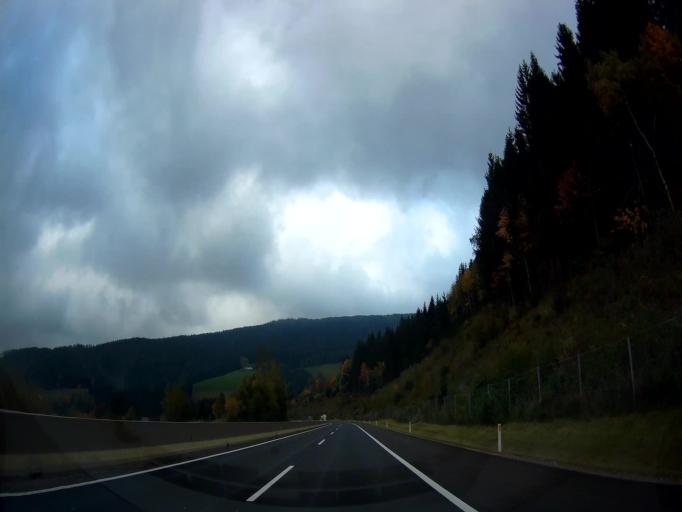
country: AT
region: Styria
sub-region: Politischer Bezirk Voitsberg
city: Modriach
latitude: 46.9674
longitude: 15.1039
